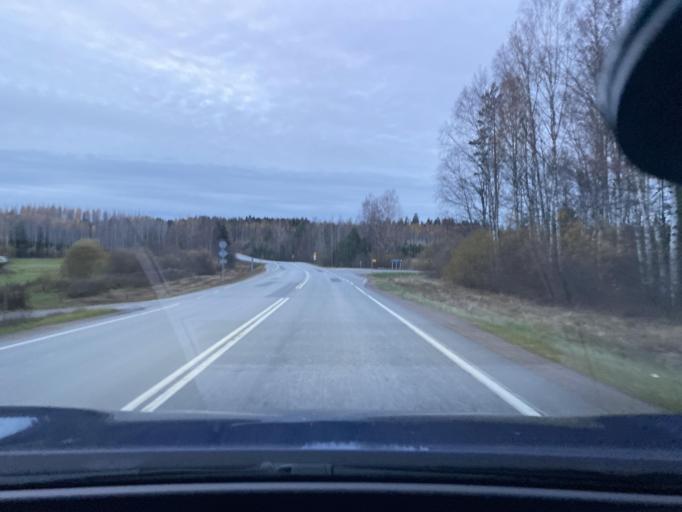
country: FI
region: Uusimaa
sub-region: Helsinki
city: Sammatti
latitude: 60.3895
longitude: 23.8127
